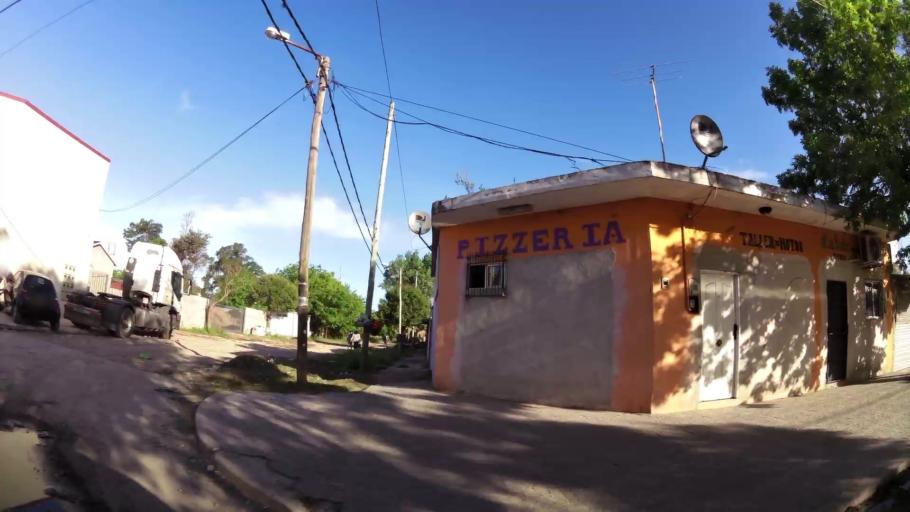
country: AR
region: Buenos Aires
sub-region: Partido de Quilmes
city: Quilmes
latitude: -34.8165
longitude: -58.2048
